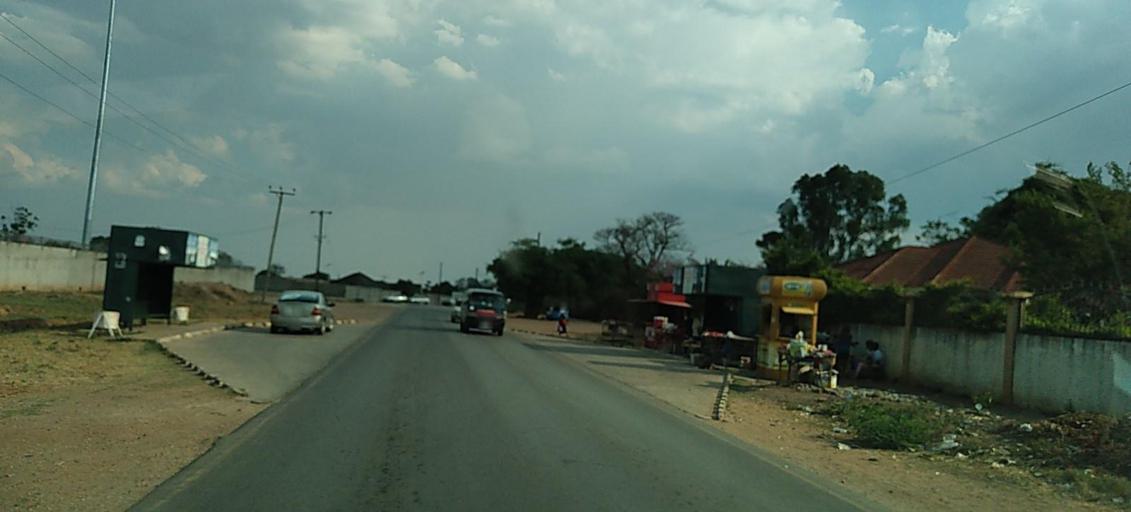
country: ZM
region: Lusaka
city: Lusaka
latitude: -15.5137
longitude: 28.2370
